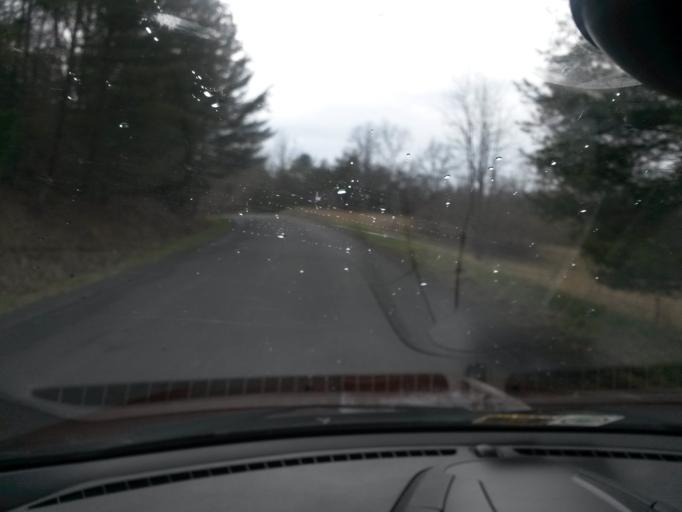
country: US
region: Virginia
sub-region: Bath County
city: Warm Springs
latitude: 38.0838
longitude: -79.8071
